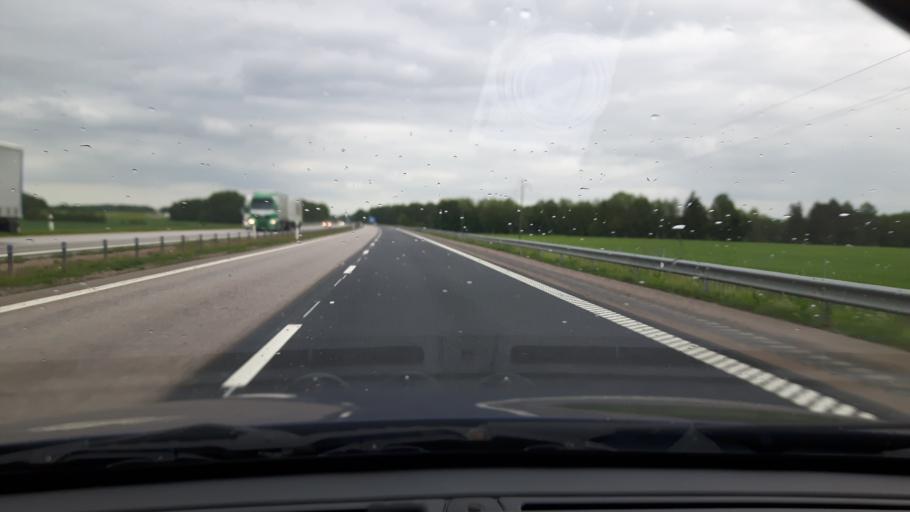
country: SE
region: OEstergoetland
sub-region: Mjolby Kommun
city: Mantorp
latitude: 58.3615
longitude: 15.2621
